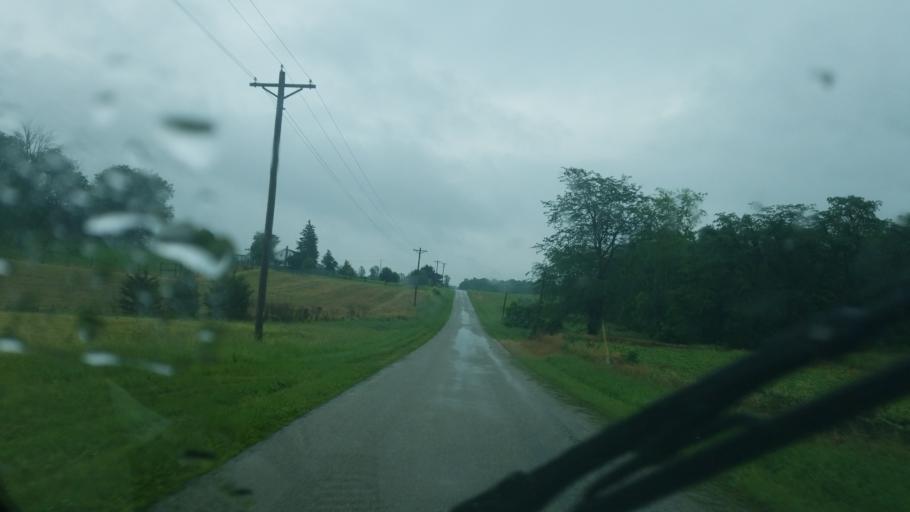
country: US
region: Ohio
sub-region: Huron County
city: Plymouth
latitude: 40.9451
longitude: -82.7330
